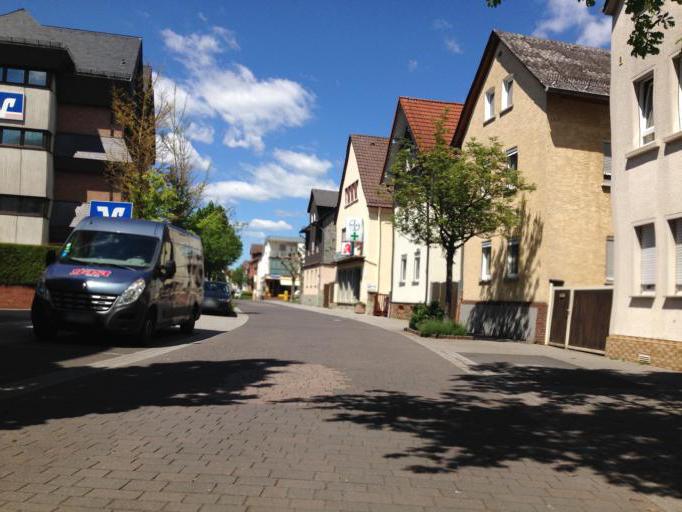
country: DE
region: Hesse
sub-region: Regierungsbezirk Giessen
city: Heuchelheim
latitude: 50.5831
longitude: 8.6333
